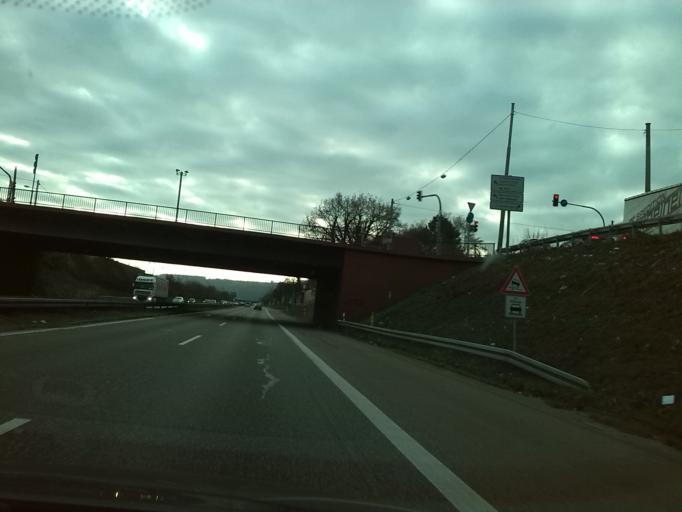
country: DE
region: Baden-Wuerttemberg
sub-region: Regierungsbezirk Stuttgart
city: Ostfildern
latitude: 48.7609
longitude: 9.2567
